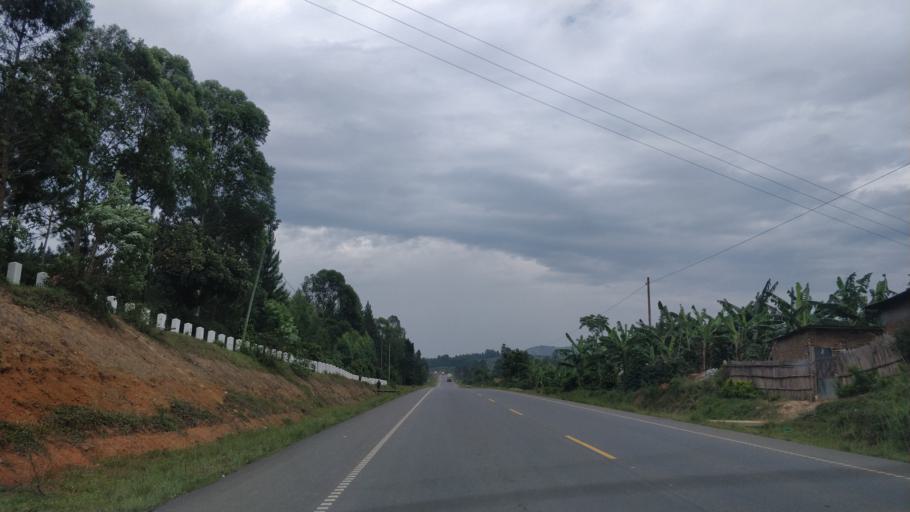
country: UG
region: Western Region
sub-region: Sheema District
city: Kibingo
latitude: -0.6701
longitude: 30.4368
